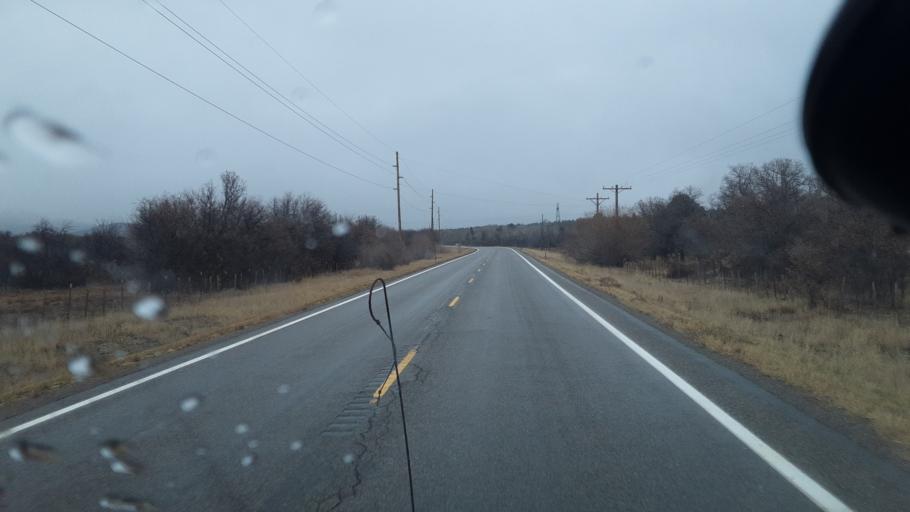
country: US
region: Colorado
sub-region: La Plata County
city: Durango
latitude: 37.2379
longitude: -108.0419
